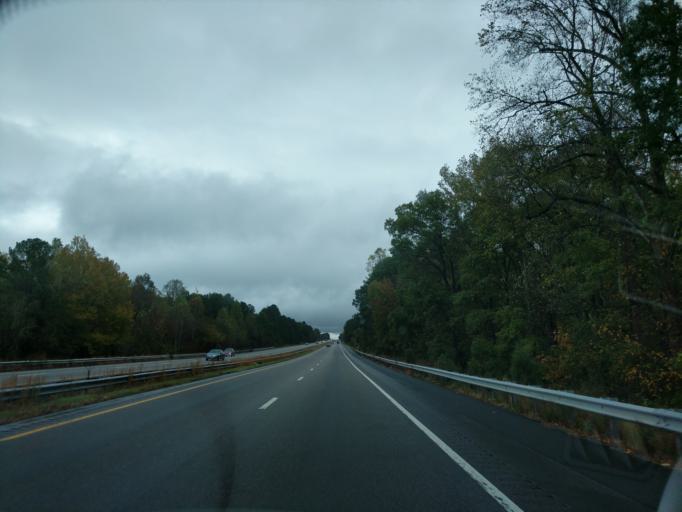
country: US
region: North Carolina
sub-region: Durham County
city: Gorman
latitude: 36.0397
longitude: -78.8254
